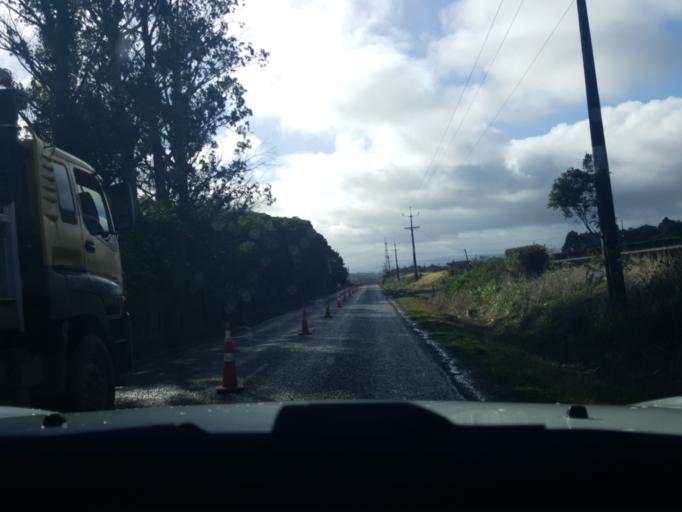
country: NZ
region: Auckland
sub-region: Auckland
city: Pukekohe East
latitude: -37.3095
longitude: 174.9896
